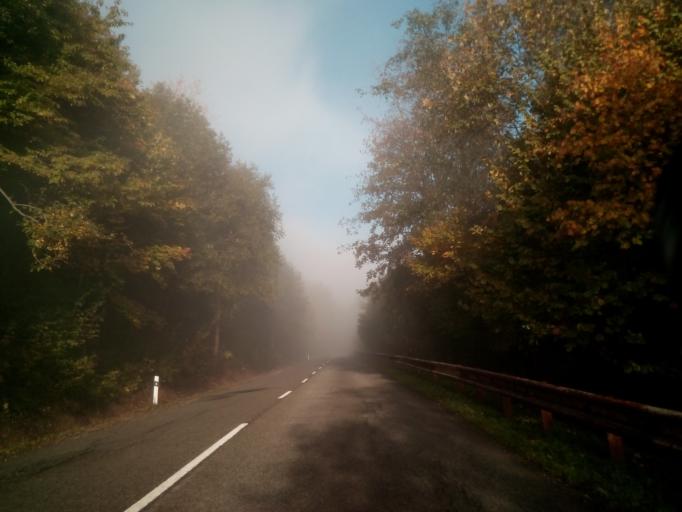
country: SK
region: Kosicky
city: Gelnica
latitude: 48.8462
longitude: 21.0350
